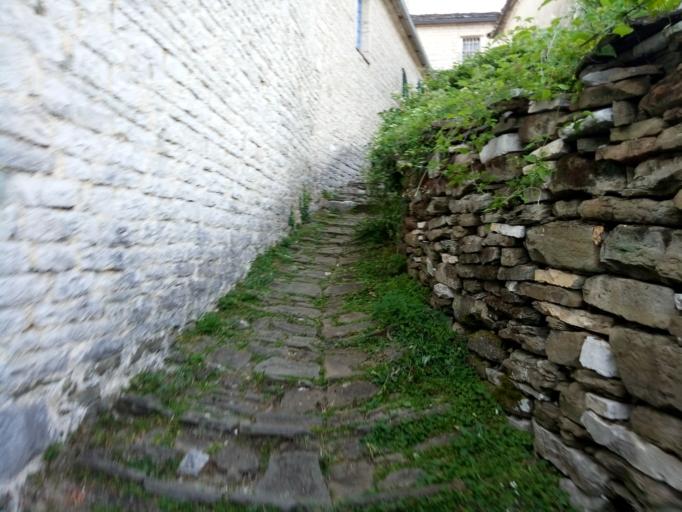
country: GR
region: Epirus
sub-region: Nomos Ioanninon
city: Asprangeloi
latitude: 39.8532
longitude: 20.7653
